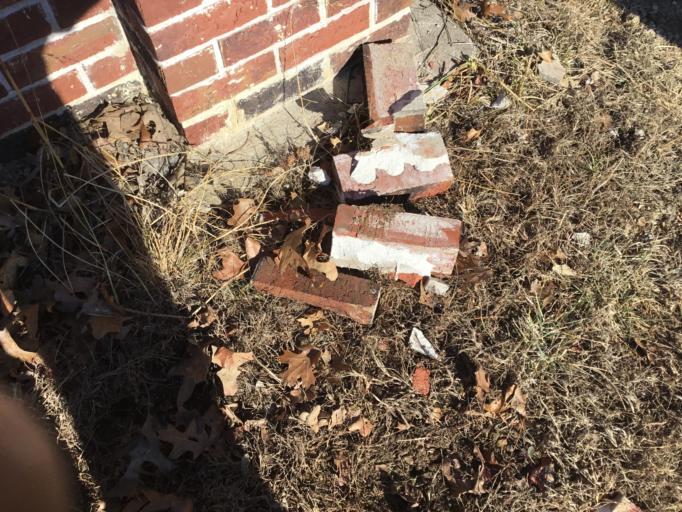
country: US
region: Missouri
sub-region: Maries County
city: Belle
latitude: 38.3536
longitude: -91.6748
